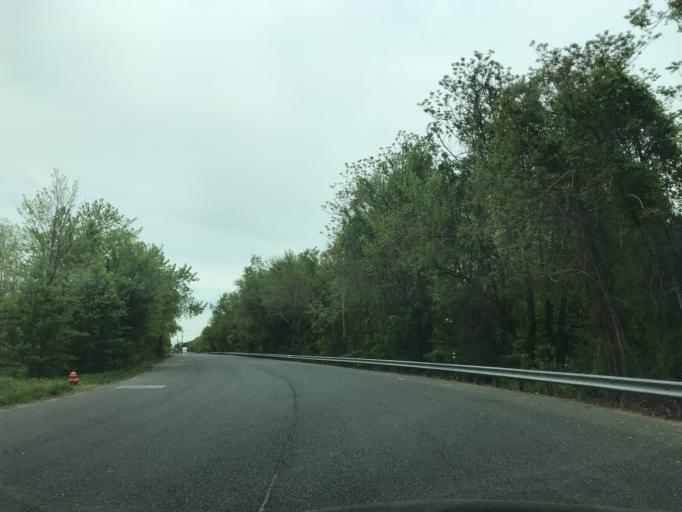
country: US
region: Maryland
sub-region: Baltimore County
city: Edgemere
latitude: 39.2530
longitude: -76.4684
